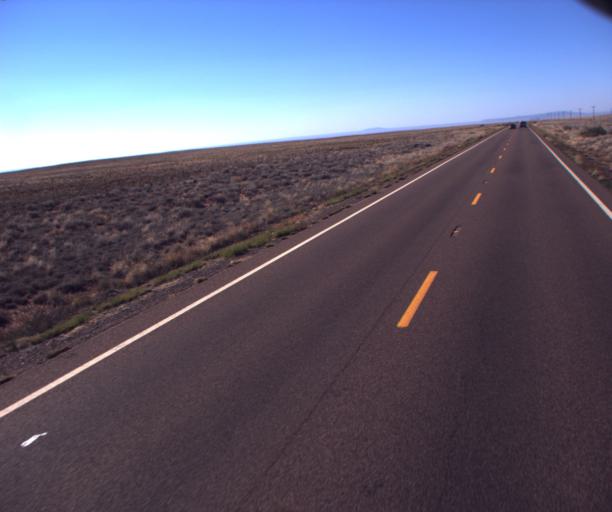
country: US
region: Arizona
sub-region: Navajo County
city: Winslow
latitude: 35.1177
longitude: -110.5127
